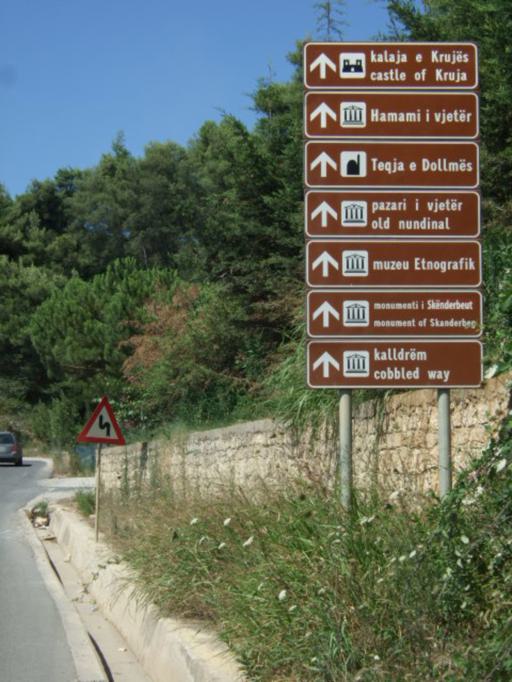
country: AL
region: Durres
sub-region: Rrethi i Krujes
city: Kruje
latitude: 41.4869
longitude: 19.7672
